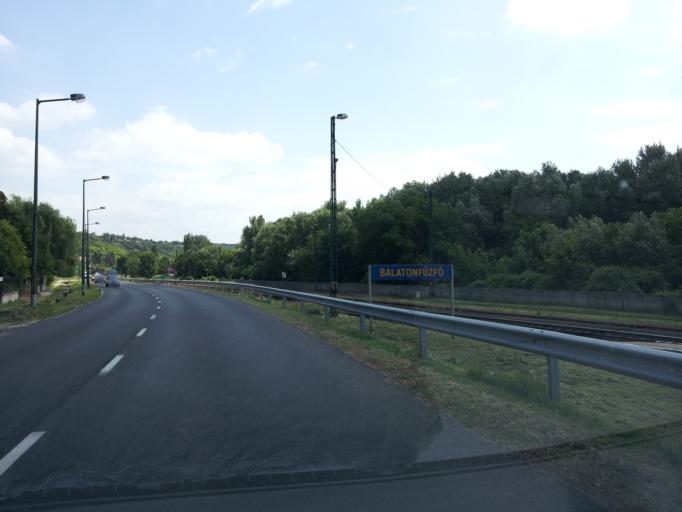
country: HU
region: Veszprem
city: Balatonalmadi
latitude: 47.0593
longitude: 18.0440
